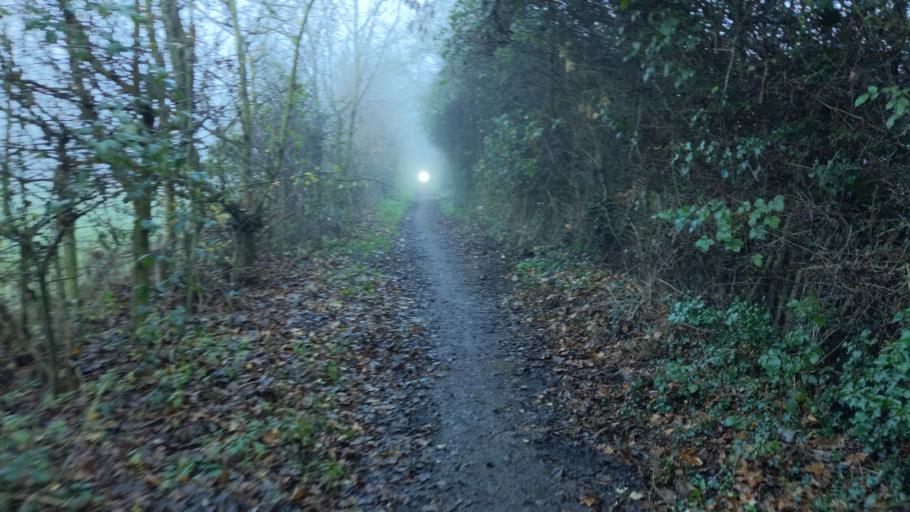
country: GB
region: England
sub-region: Milton Keynes
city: Water Eaton
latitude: 51.9990
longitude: -0.7098
